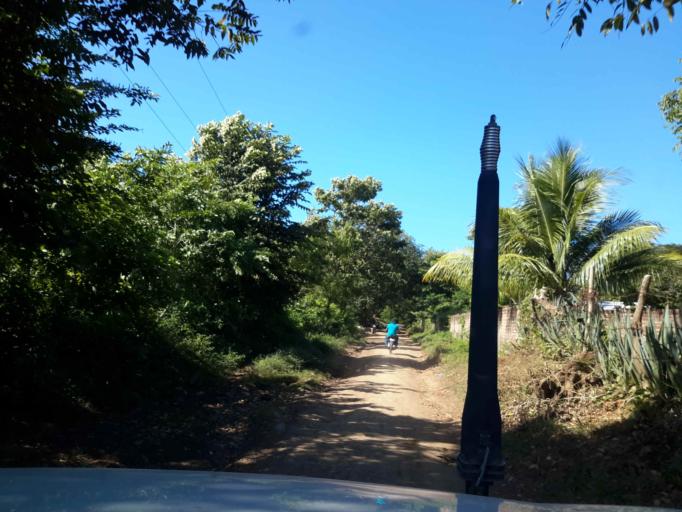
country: NI
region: Rivas
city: Tola
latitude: 11.4626
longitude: -85.9497
